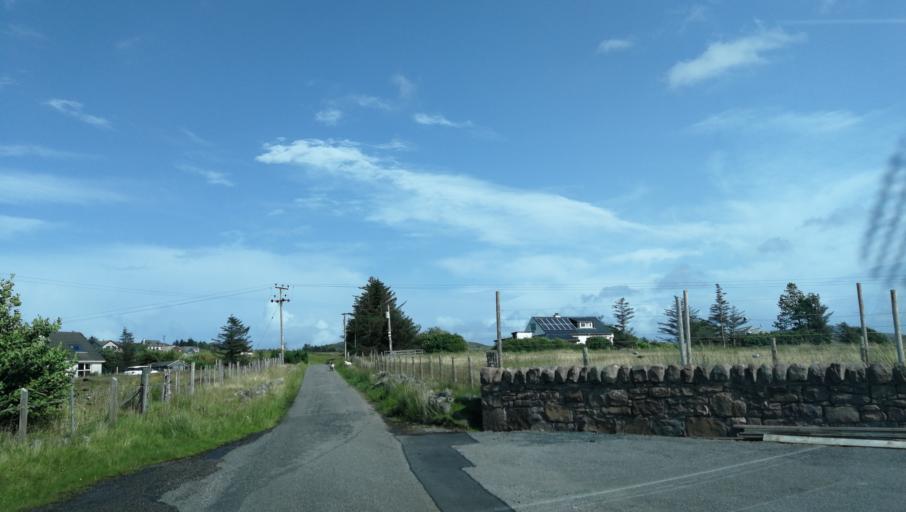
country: GB
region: Scotland
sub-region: Highland
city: Portree
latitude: 57.7448
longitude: -5.7753
